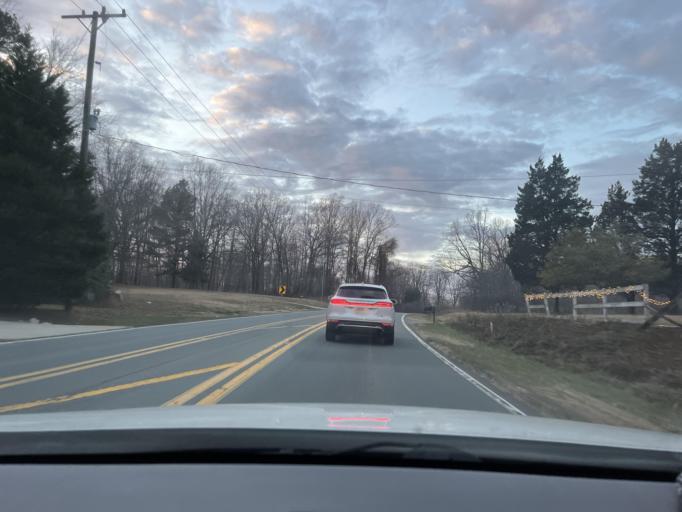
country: US
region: North Carolina
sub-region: Guilford County
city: McLeansville
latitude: 36.0704
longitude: -79.6308
